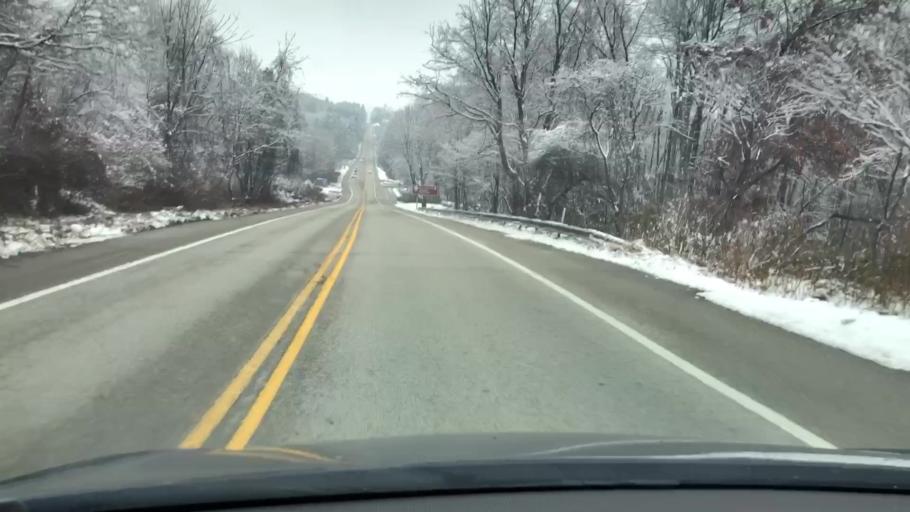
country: US
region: Pennsylvania
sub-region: Fayette County
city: Hopwood
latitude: 39.8175
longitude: -79.5865
